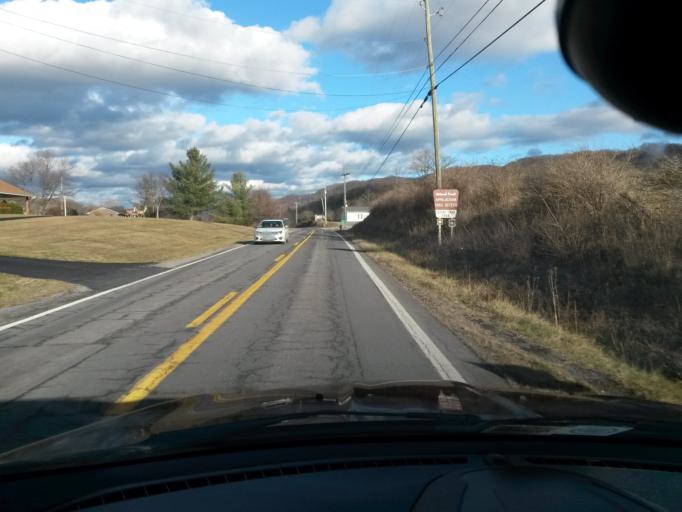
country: US
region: Virginia
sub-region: Giles County
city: Pearisburg
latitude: 37.4333
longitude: -80.7060
